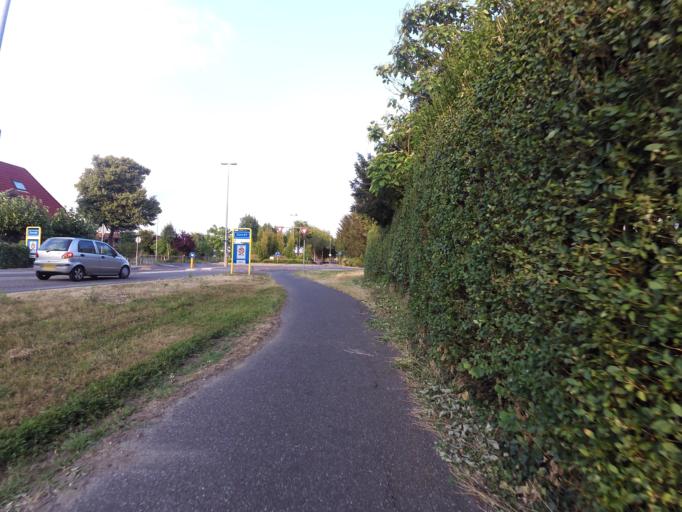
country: NL
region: Gelderland
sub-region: Gemeente Groesbeek
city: Berg en Dal
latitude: 51.8785
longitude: 5.9568
